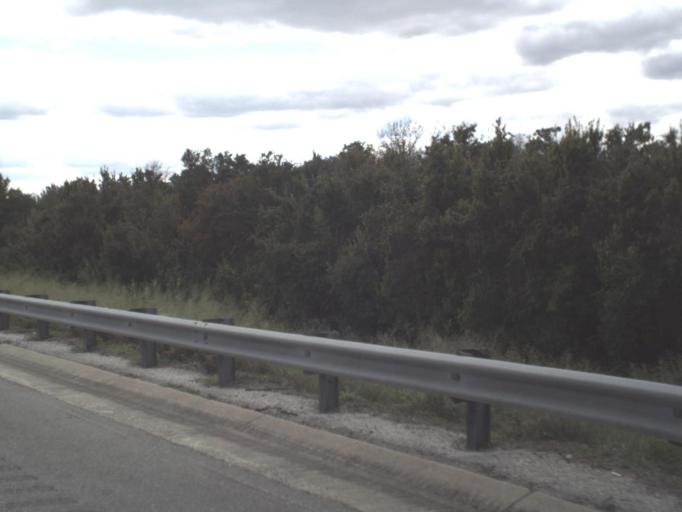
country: US
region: Florida
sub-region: Osceola County
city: Saint Cloud
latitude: 28.2644
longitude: -81.3332
